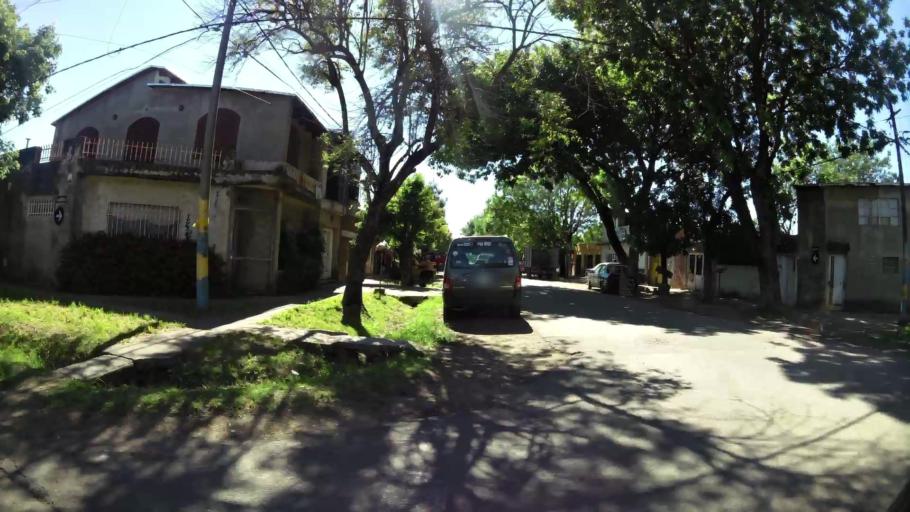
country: AR
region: Santa Fe
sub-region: Departamento de Rosario
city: Rosario
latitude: -32.9659
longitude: -60.6962
